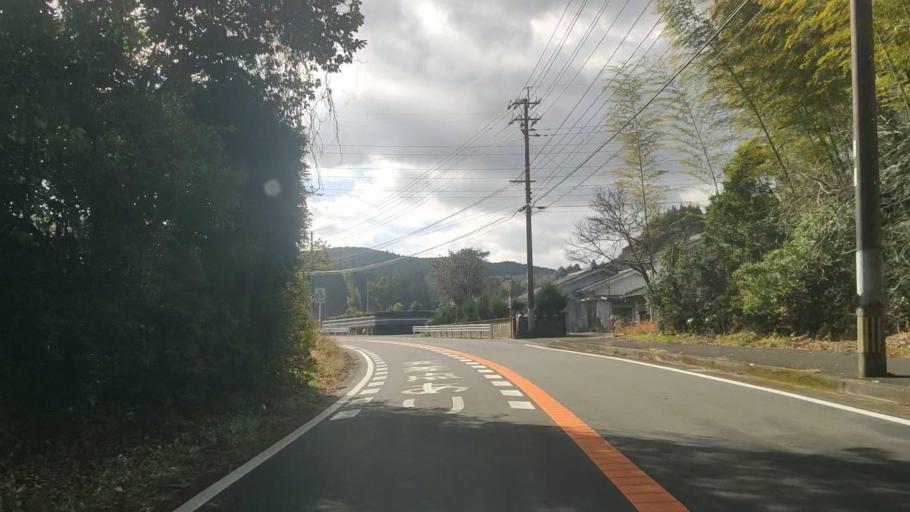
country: JP
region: Kagoshima
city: Okuchi-shinohara
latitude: 31.9346
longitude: 130.7034
